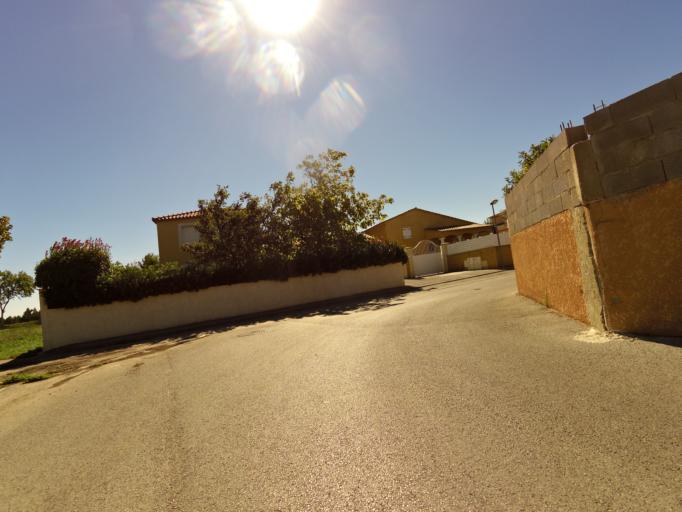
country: FR
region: Languedoc-Roussillon
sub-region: Departement du Gard
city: Codognan
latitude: 43.7312
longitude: 4.2263
